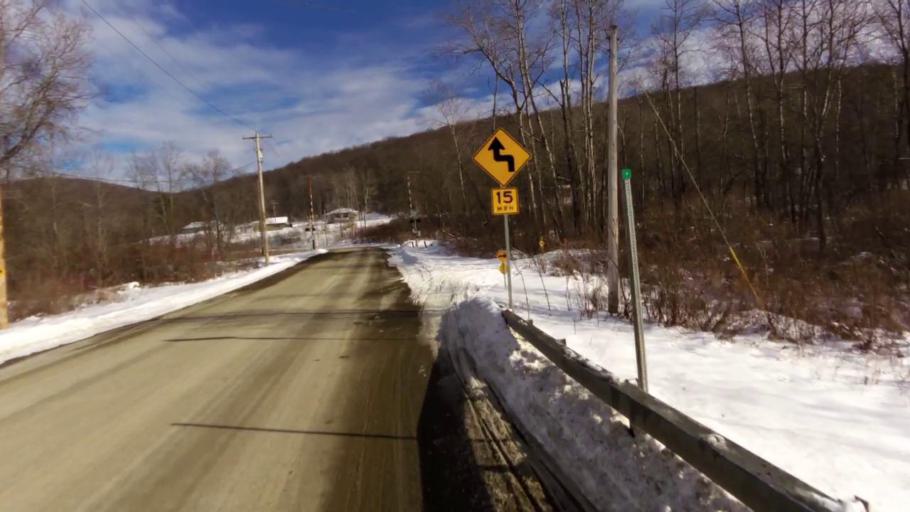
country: US
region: Pennsylvania
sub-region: McKean County
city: Foster Brook
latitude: 42.0641
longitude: -78.6386
